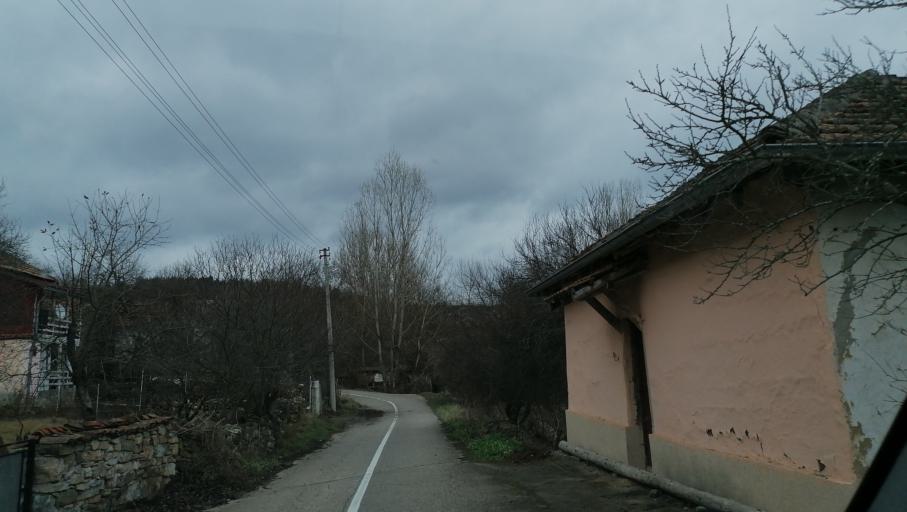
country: RS
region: Central Serbia
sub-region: Pirotski Okrug
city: Dimitrovgrad
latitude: 42.9258
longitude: 22.7665
